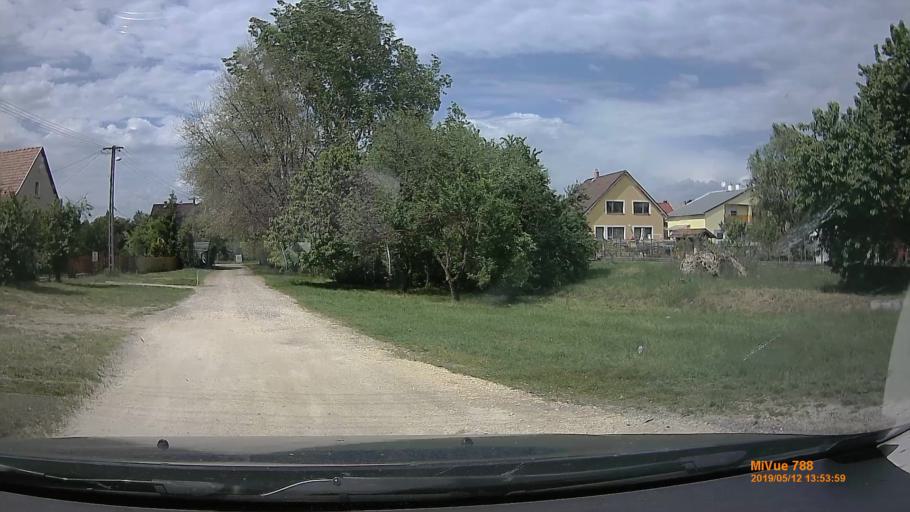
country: HU
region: Pest
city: Pecel
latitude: 47.4884
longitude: 19.2982
